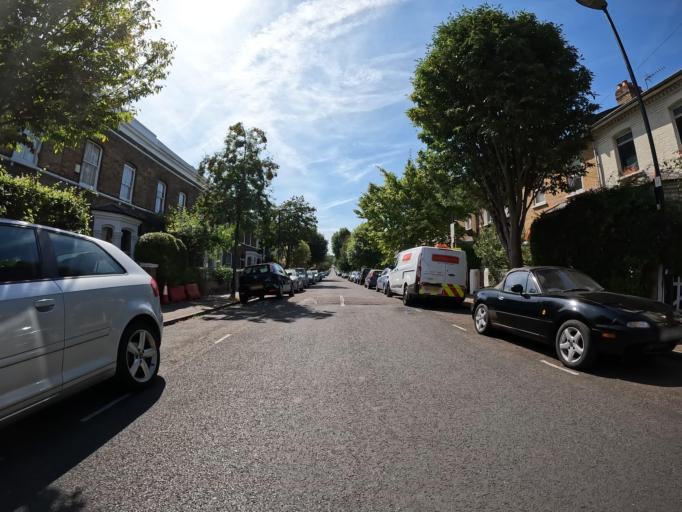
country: GB
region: England
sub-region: Greater London
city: Harringay
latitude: 51.5604
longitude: -0.1033
